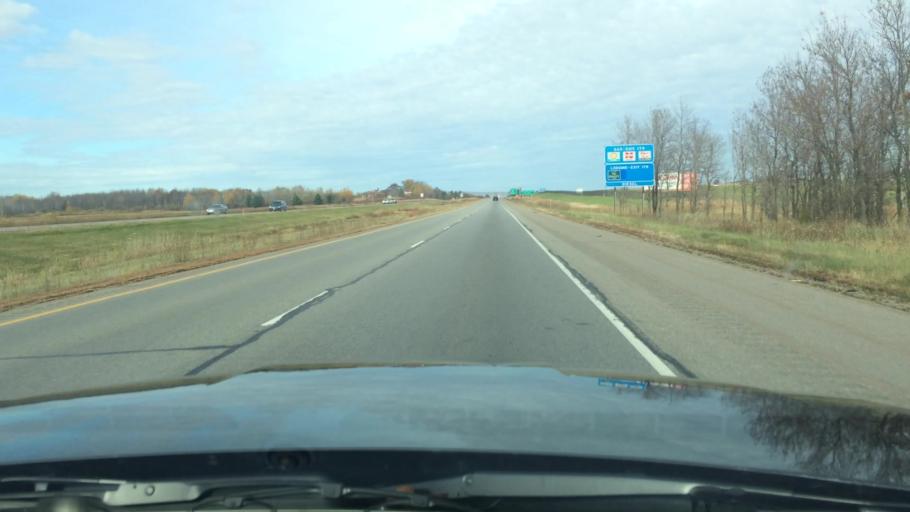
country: US
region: Wisconsin
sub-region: Marathon County
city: Mosinee
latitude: 44.7755
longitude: -89.6801
